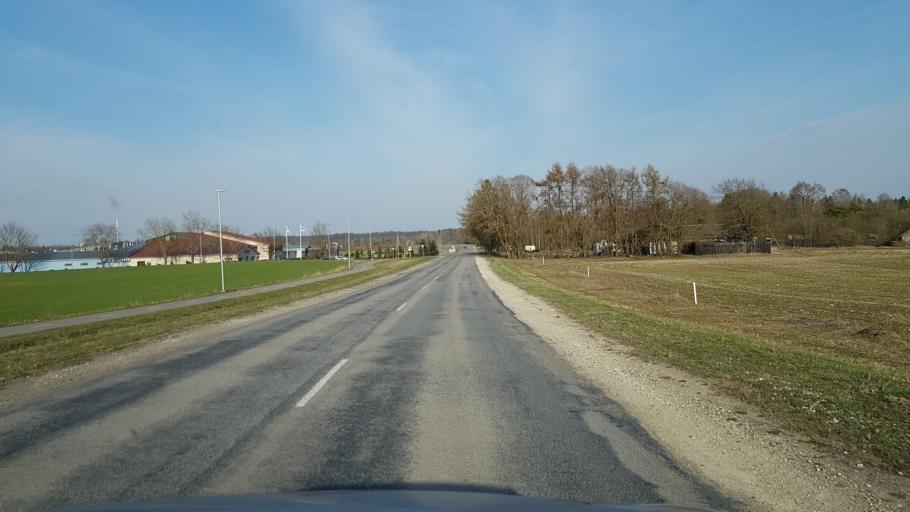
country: EE
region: Laeaene-Virumaa
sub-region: Rakvere linn
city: Rakvere
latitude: 59.3332
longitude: 26.3130
